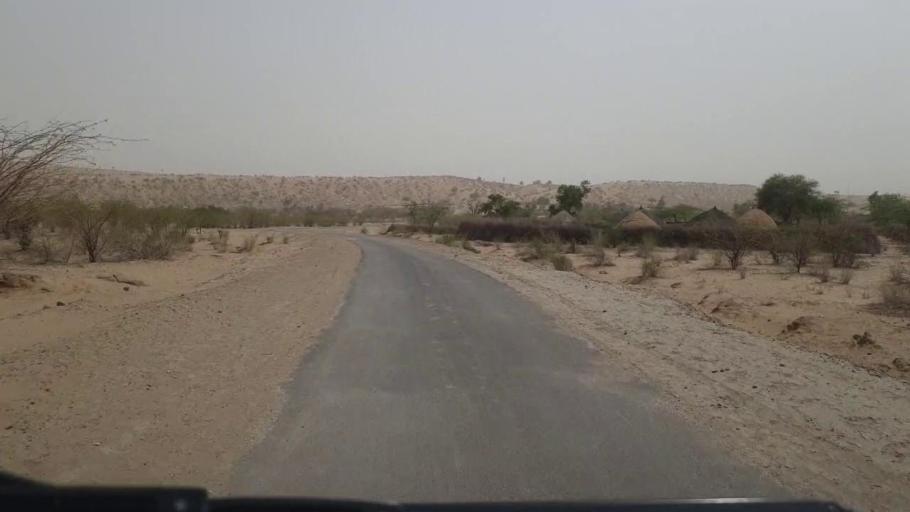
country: PK
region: Sindh
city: Islamkot
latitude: 25.2658
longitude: 70.6492
